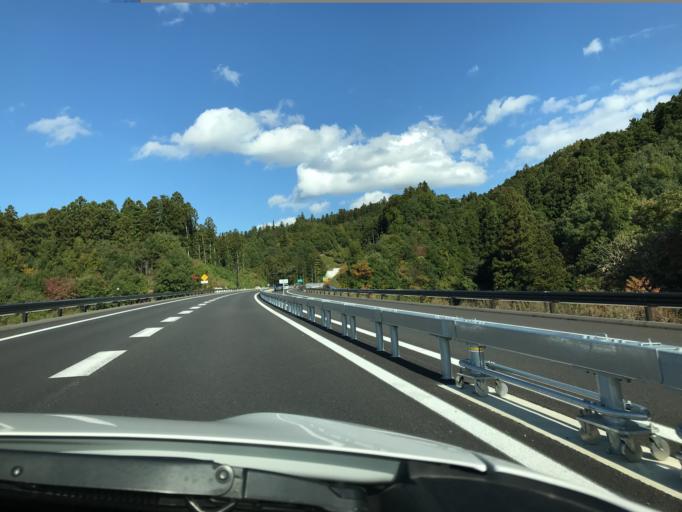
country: JP
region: Fukushima
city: Yanagawamachi-saiwaicho
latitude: 37.7524
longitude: 140.6479
